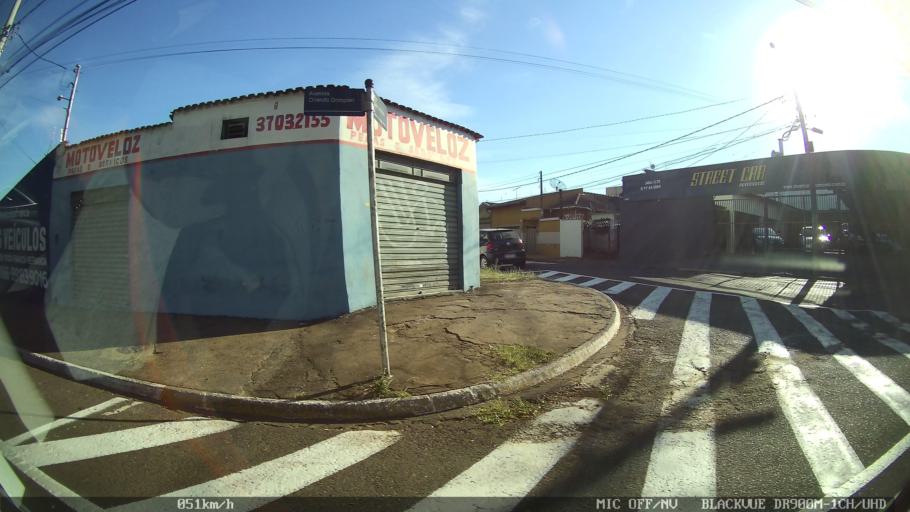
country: BR
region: Sao Paulo
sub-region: Franca
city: Franca
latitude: -20.5117
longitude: -47.3996
